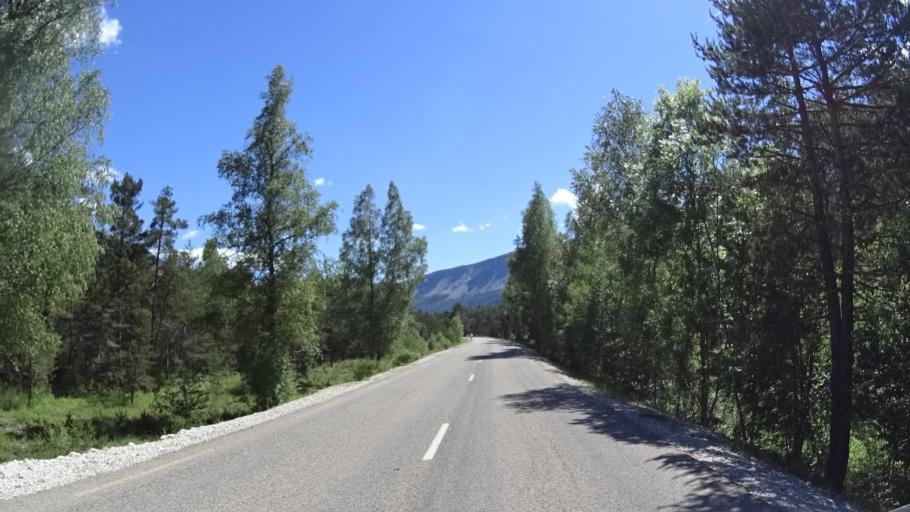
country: FR
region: Provence-Alpes-Cote d'Azur
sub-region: Departement des Alpes-de-Haute-Provence
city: Annot
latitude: 44.1564
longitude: 6.6007
